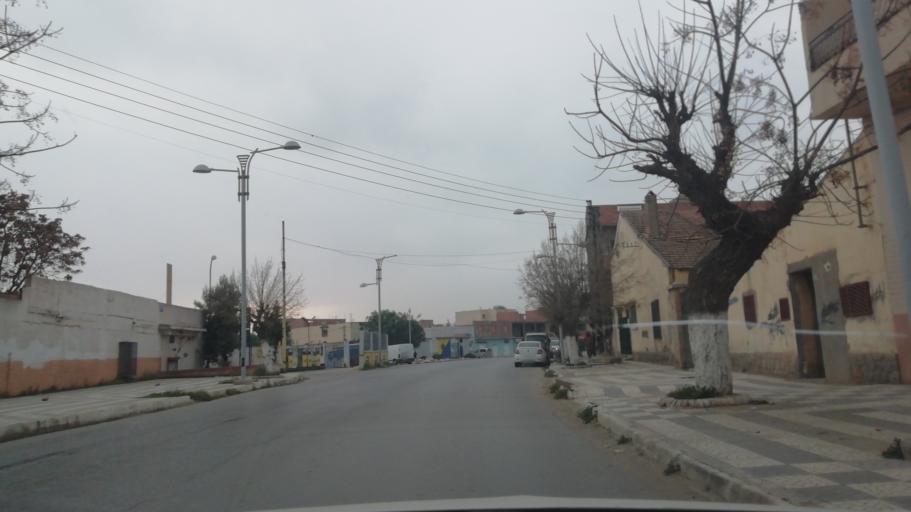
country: DZ
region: Sidi Bel Abbes
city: Sfizef
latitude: 35.2332
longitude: -0.2455
